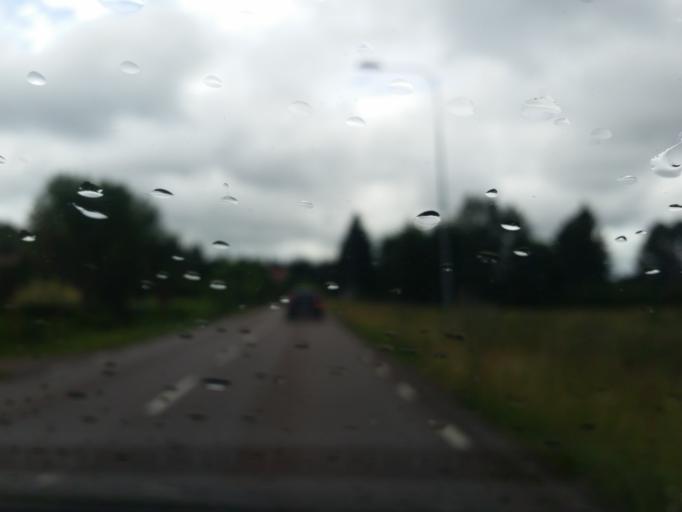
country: SE
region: Dalarna
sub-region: Leksand Municipality
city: Leksand
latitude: 60.7180
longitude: 14.9671
